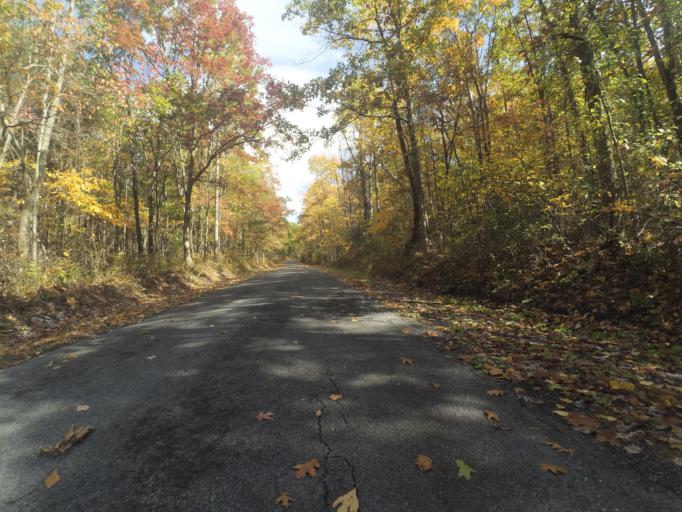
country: US
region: Pennsylvania
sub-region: Centre County
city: Park Forest Village
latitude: 40.8920
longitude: -77.9513
